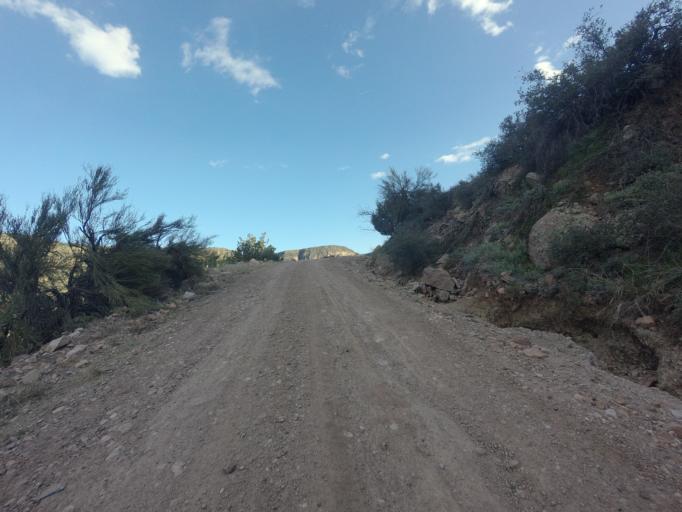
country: US
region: Arizona
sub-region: Gila County
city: Pine
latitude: 34.3745
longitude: -111.6636
